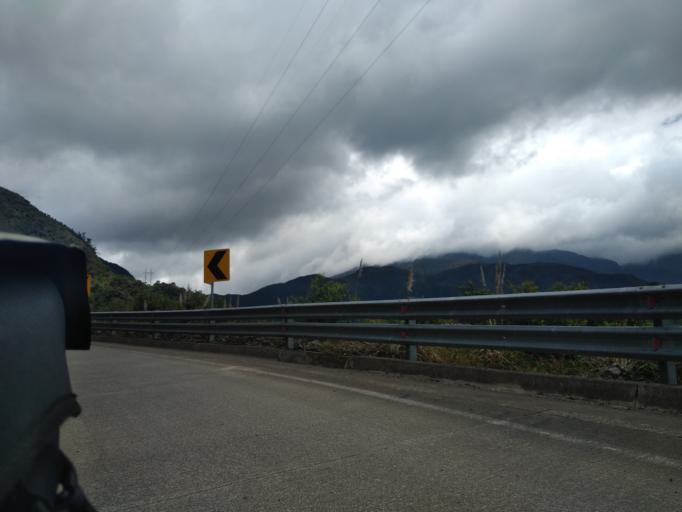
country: EC
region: Zamora-Chinchipe
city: Zamora
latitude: -4.4322
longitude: -79.1501
